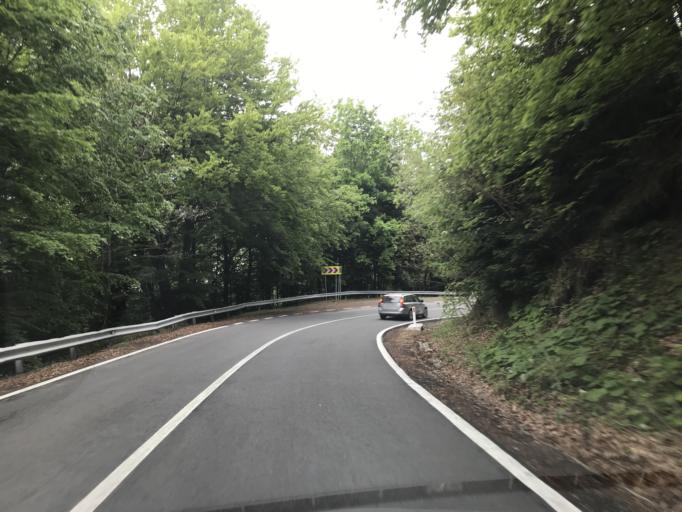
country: RO
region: Sibiu
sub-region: Comuna Cartisoara
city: Cartisoara
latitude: 45.6719
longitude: 24.5882
